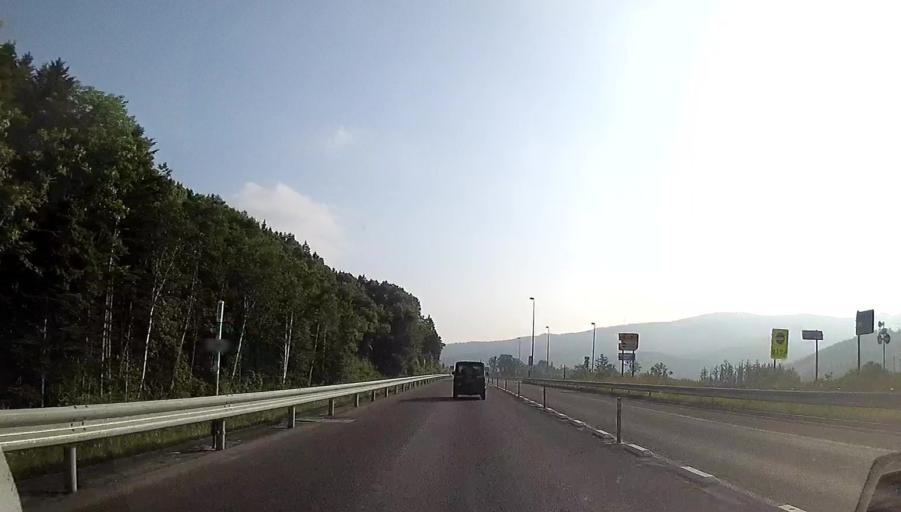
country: JP
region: Hokkaido
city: Shimo-furano
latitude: 43.0090
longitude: 142.4223
